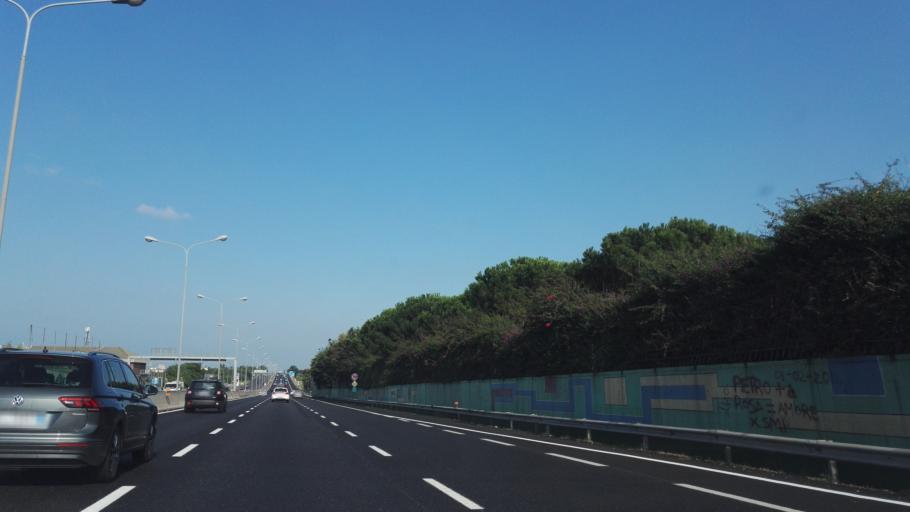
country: IT
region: Apulia
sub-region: Provincia di Bari
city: Bari
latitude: 41.0895
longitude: 16.8724
